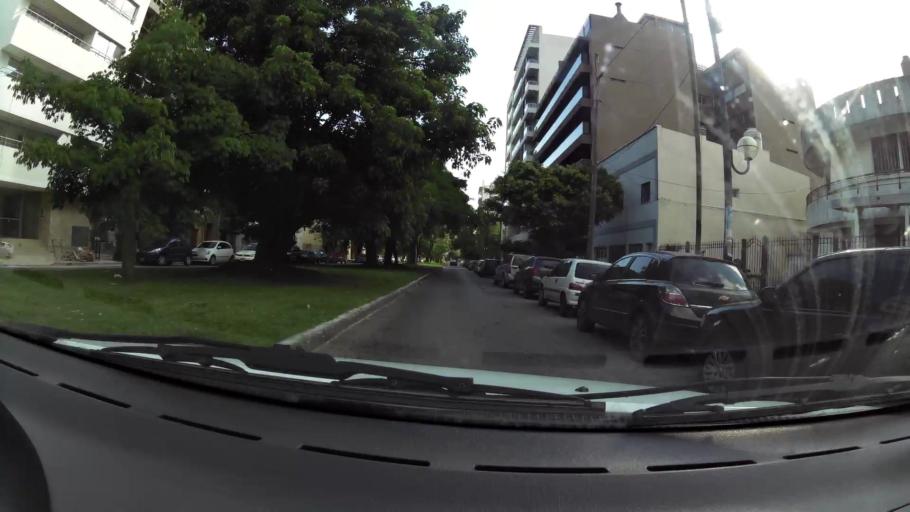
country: AR
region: Buenos Aires
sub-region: Partido de La Plata
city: La Plata
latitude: -34.9038
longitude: -57.9602
